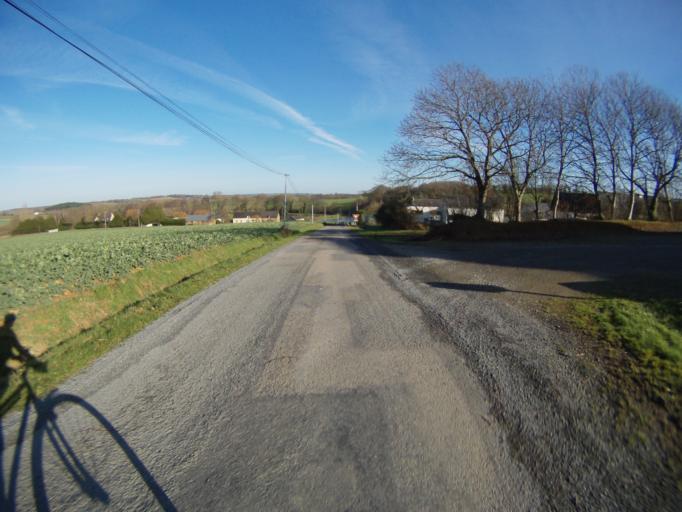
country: FR
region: Brittany
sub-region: Departement d'Ille-et-Vilaine
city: Chanteloup
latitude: 47.9384
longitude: -1.6058
